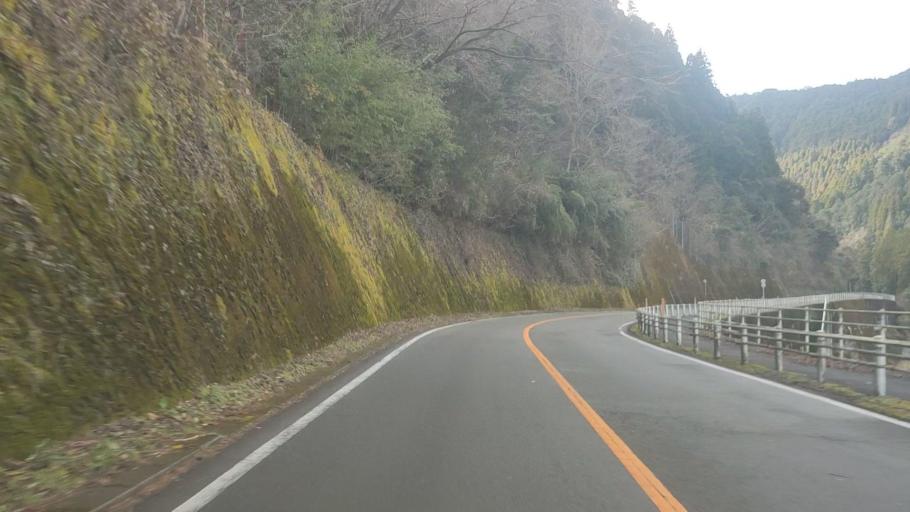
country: JP
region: Kumamoto
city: Hitoyoshi
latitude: 32.2937
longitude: 130.8452
